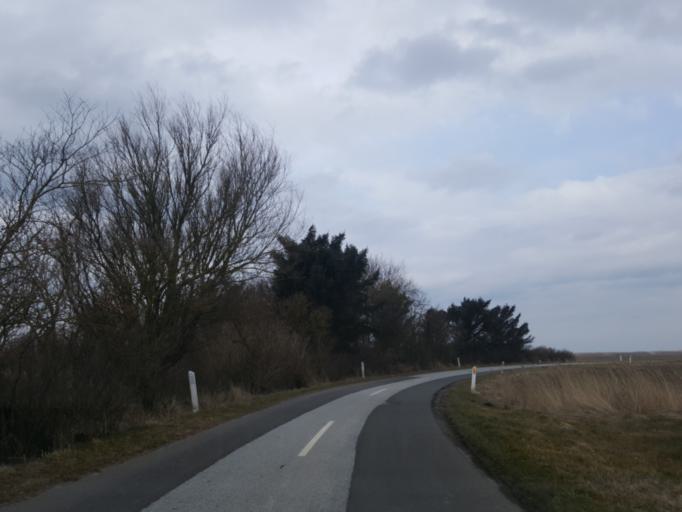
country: DK
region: Central Jutland
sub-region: Lemvig Kommune
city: Harboore
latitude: 56.4396
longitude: 8.1419
